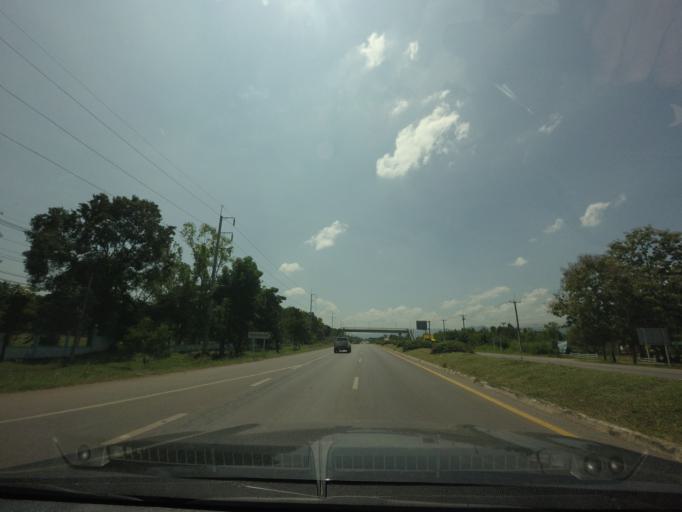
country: TH
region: Phetchabun
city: Lom Sak
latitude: 16.7276
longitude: 101.1874
